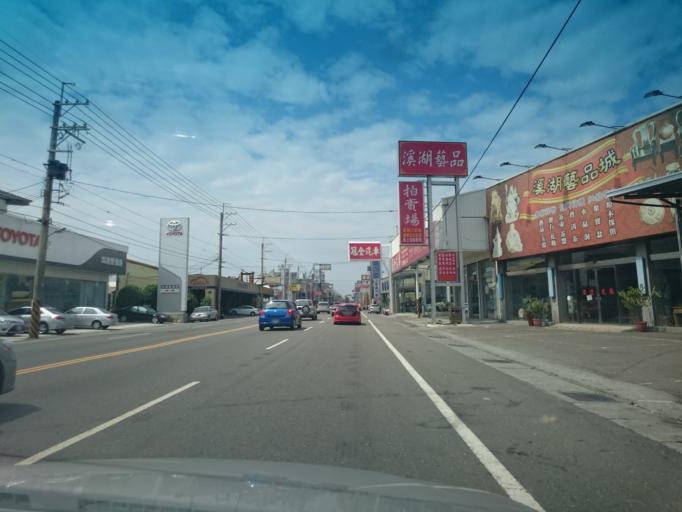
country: TW
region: Taiwan
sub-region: Changhua
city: Chang-hua
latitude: 23.9553
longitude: 120.4895
